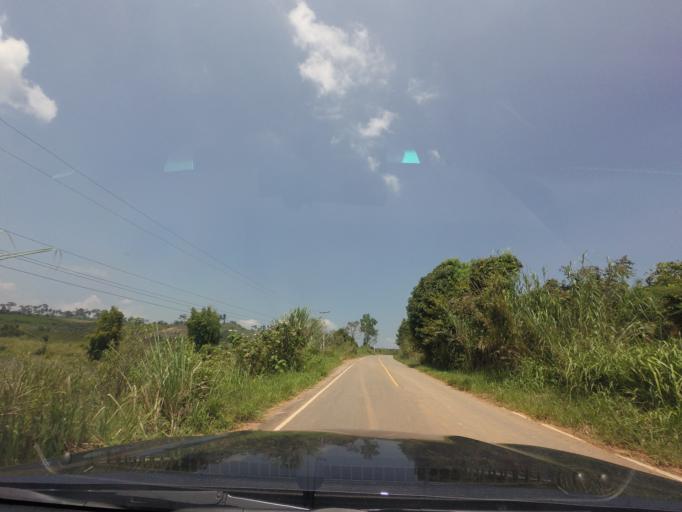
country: TH
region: Loei
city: Na Haeo
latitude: 17.5333
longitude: 100.8789
